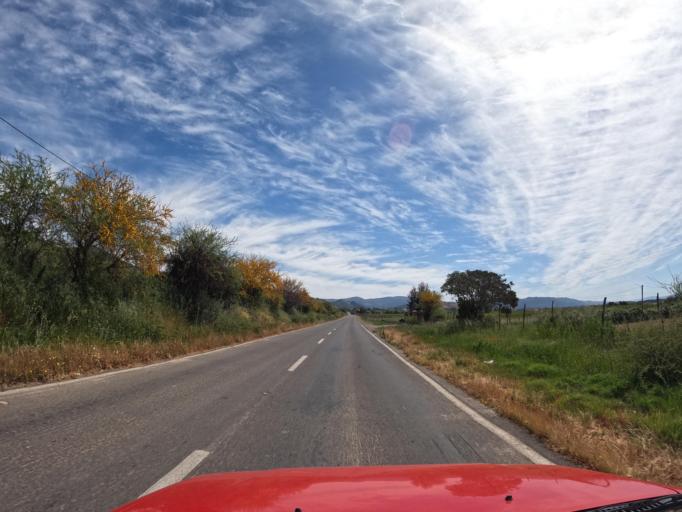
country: CL
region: Maule
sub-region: Provincia de Talca
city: Talca
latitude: -35.1217
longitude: -71.6592
